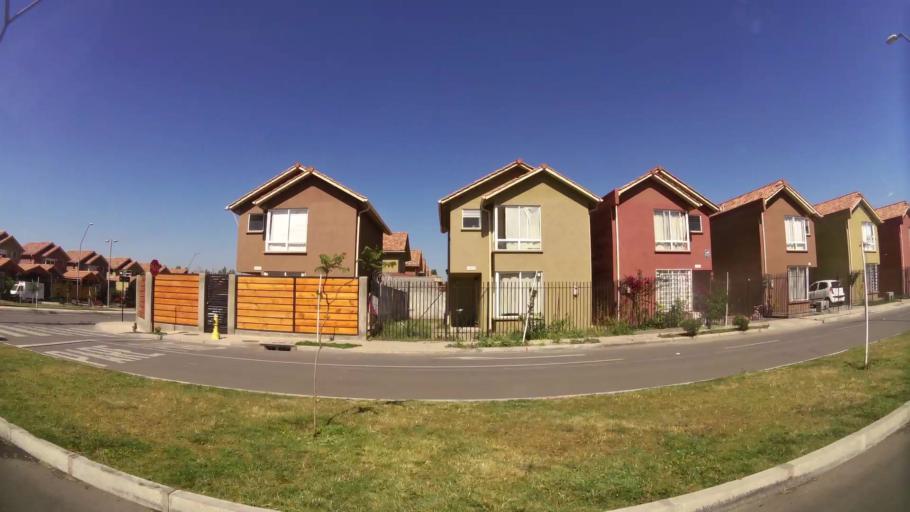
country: CL
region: Santiago Metropolitan
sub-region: Provincia de Maipo
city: San Bernardo
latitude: -33.6140
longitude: -70.6808
